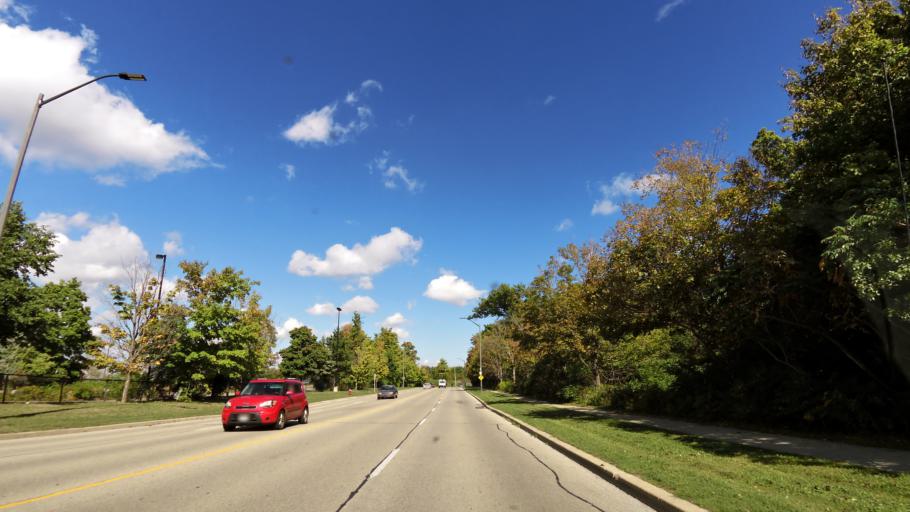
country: CA
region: Ontario
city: Brampton
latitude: 43.6003
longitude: -79.7673
